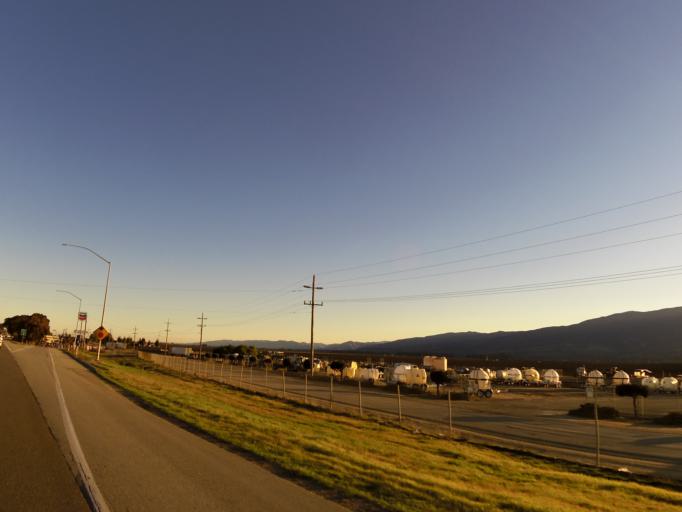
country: US
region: California
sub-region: Monterey County
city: Soledad
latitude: 36.4520
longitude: -121.3676
